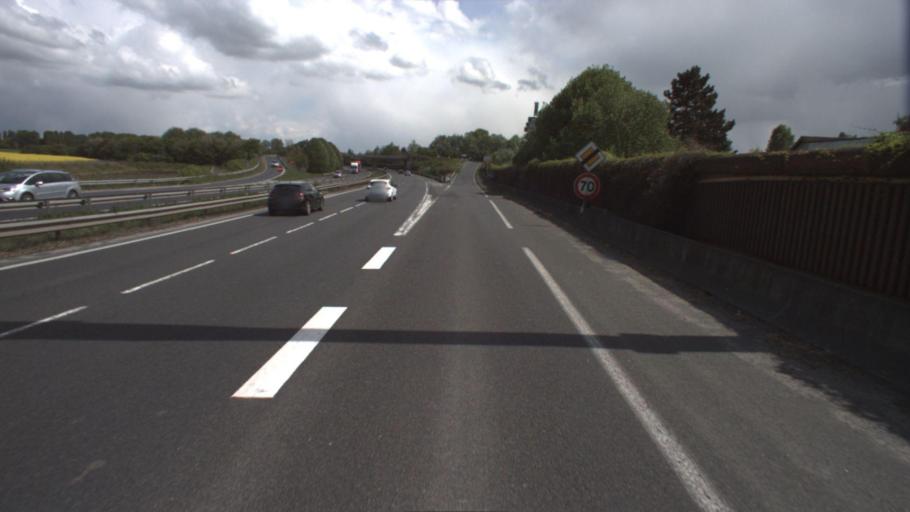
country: FR
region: Ile-de-France
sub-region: Departement de Seine-et-Marne
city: Fontenay-Tresigny
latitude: 48.7136
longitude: 2.8546
